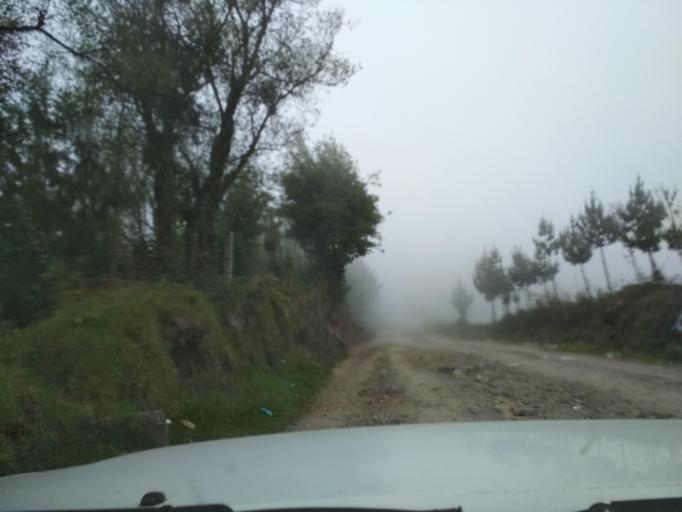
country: MX
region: Veracruz
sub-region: La Perla
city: Chilapa
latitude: 18.9816
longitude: -97.1928
